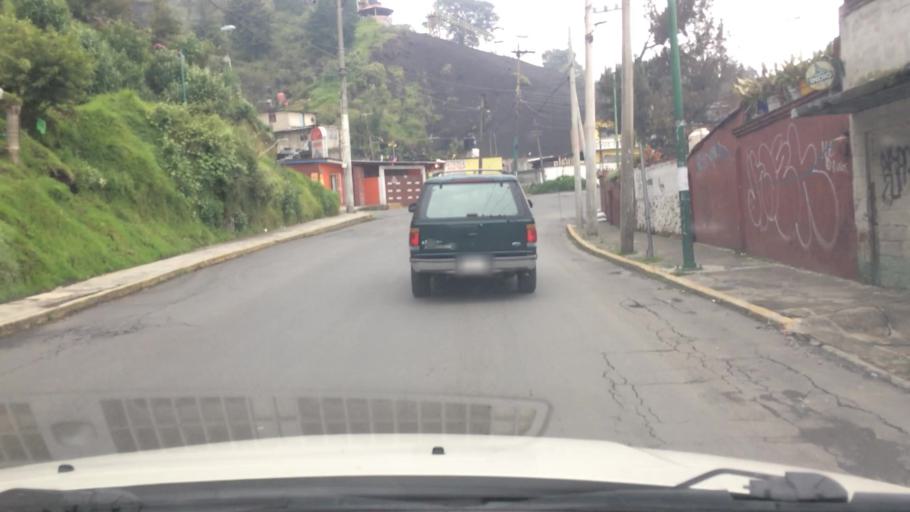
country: MX
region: Mexico City
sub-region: Tlalpan
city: Lomas de Tepemecatl
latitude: 19.2339
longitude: -99.1833
